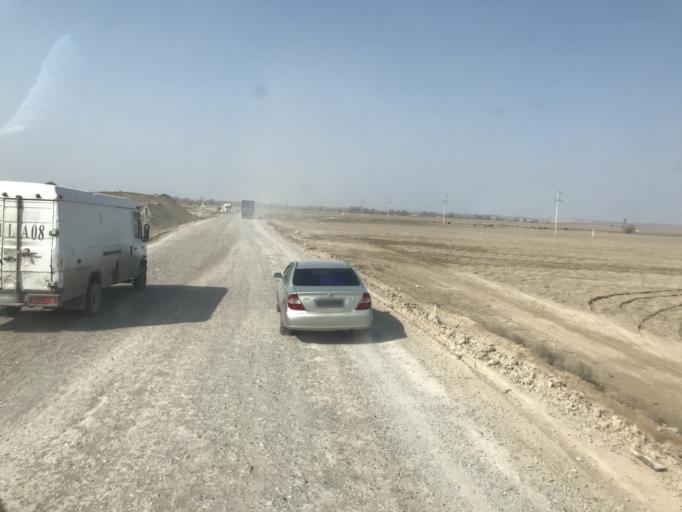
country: KG
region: Chuy
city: Bystrovka
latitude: 43.3228
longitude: 76.0398
